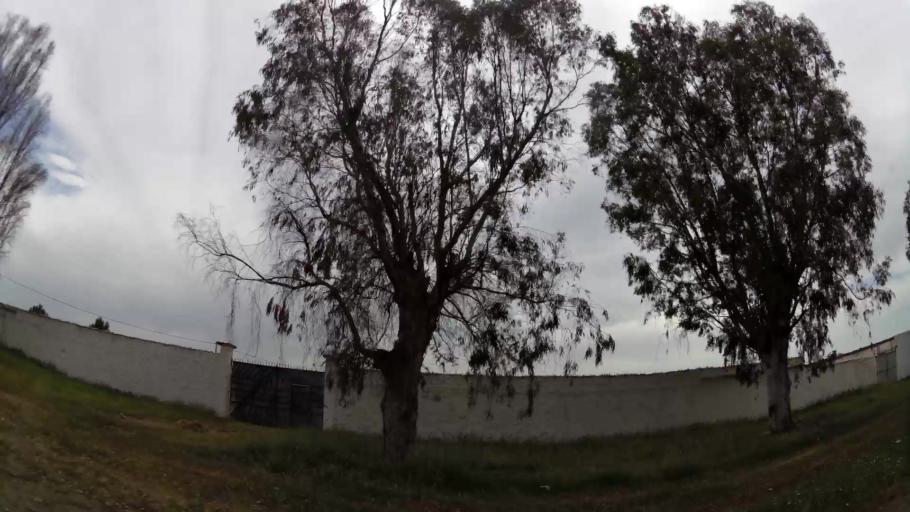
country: MA
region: Rabat-Sale-Zemmour-Zaer
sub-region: Khemisset
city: Tiflet
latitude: 33.8722
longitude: -6.2784
